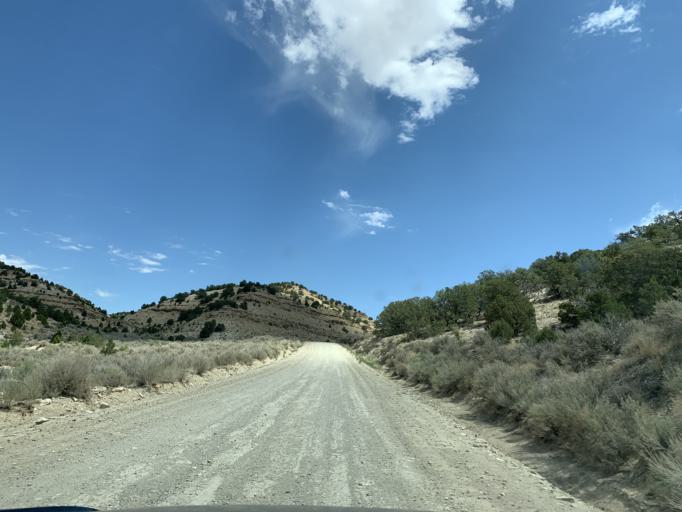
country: US
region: Utah
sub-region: Duchesne County
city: Duchesne
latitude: 39.8691
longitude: -110.2484
